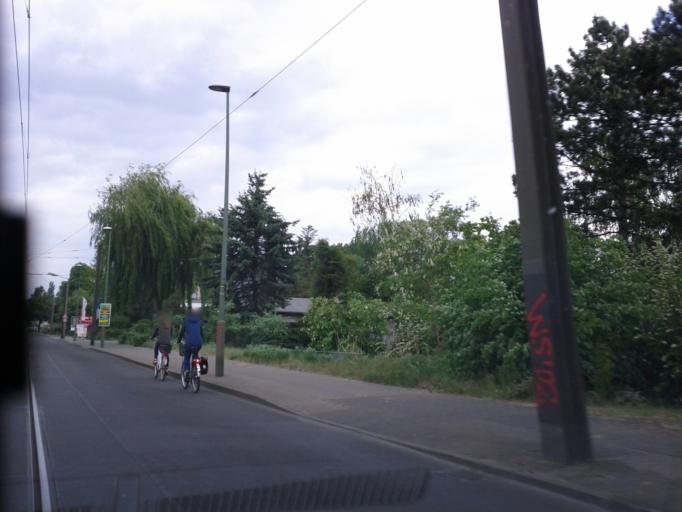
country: DE
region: Berlin
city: Berlin Koepenick
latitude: 52.4535
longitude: 13.5931
